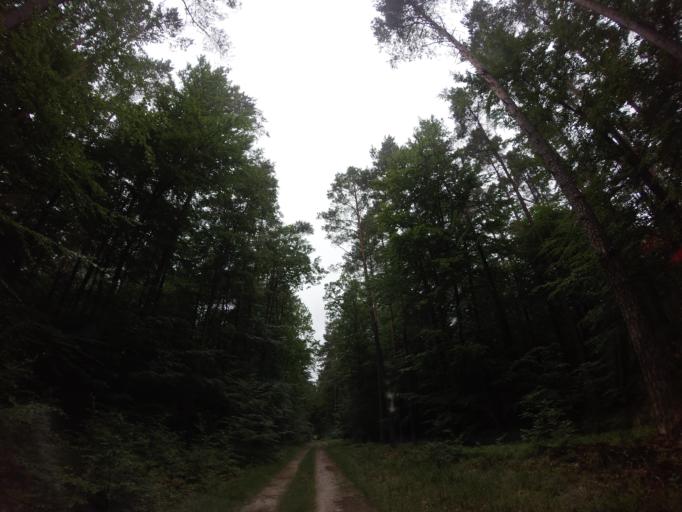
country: PL
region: West Pomeranian Voivodeship
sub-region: Powiat choszczenski
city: Drawno
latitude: 53.0990
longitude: 15.8305
